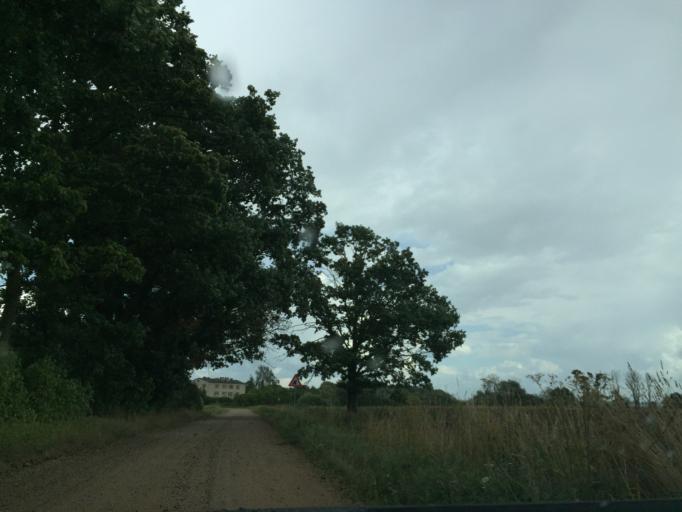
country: LV
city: Tervete
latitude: 56.3667
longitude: 23.4859
